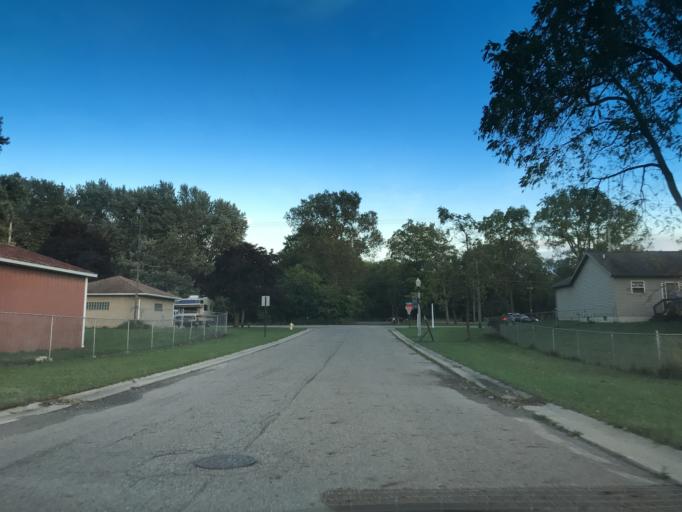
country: US
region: Michigan
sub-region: Eaton County
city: Waverly
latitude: 42.6932
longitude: -84.6321
